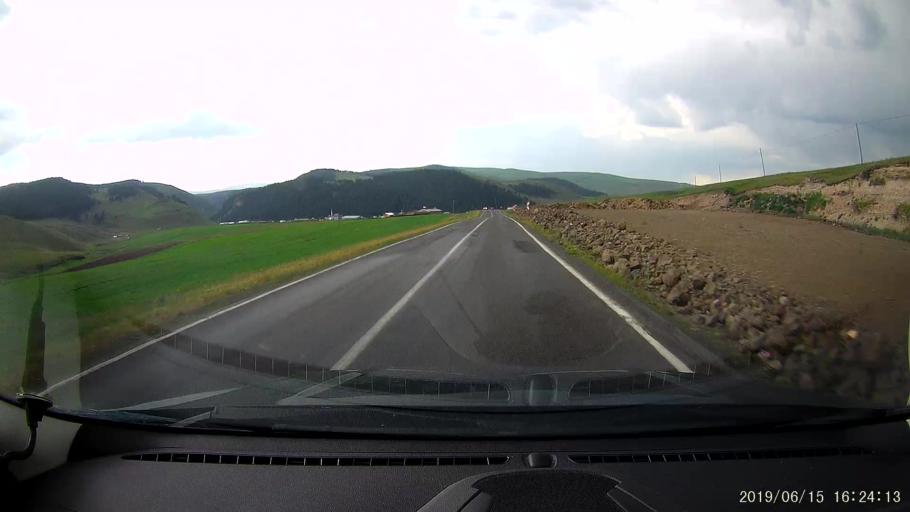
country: TR
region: Ardahan
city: Hanak
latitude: 41.1673
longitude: 42.8691
